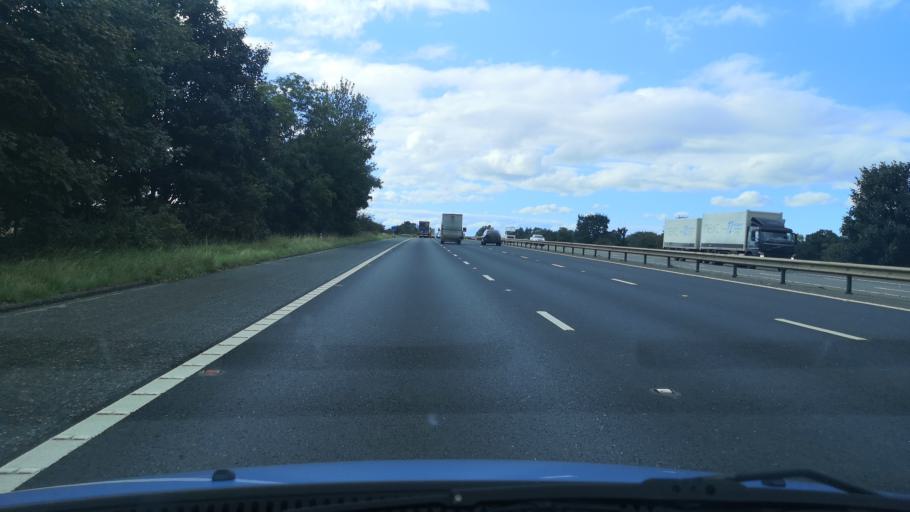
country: GB
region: England
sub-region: East Riding of Yorkshire
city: Pollington
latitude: 53.6868
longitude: -1.0939
